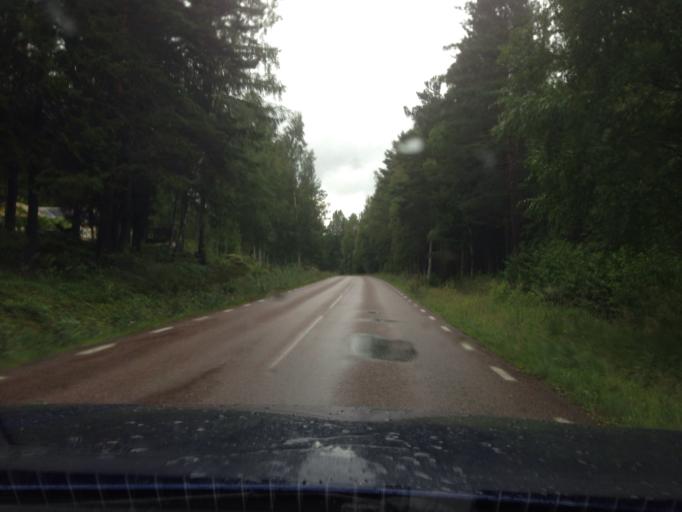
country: SE
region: Dalarna
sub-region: Ludvika Kommun
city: Grangesberg
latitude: 60.1825
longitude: 14.9725
